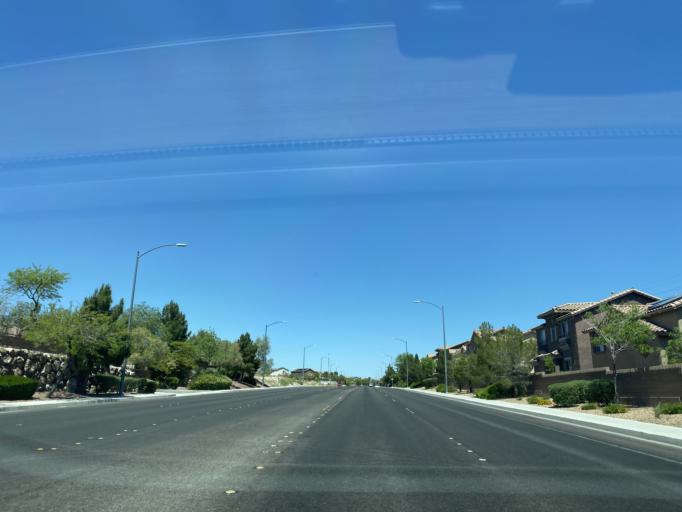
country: US
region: Nevada
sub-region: Clark County
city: Summerlin South
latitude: 36.2334
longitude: -115.3308
